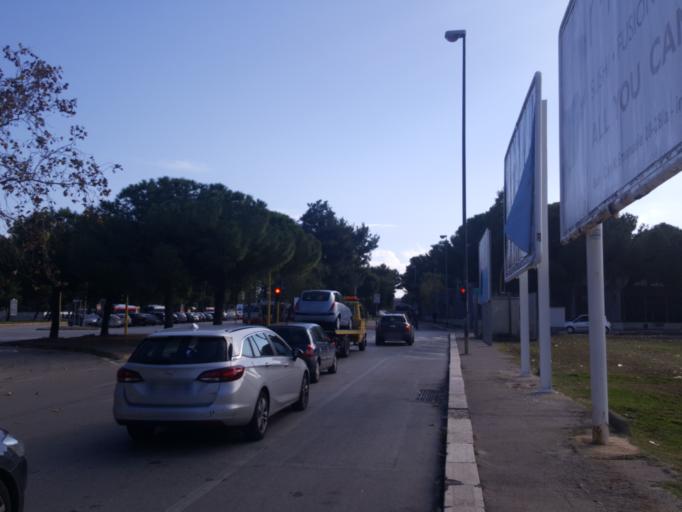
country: IT
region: Apulia
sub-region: Provincia di Bari
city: Triggiano
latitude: 41.1027
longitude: 16.9080
